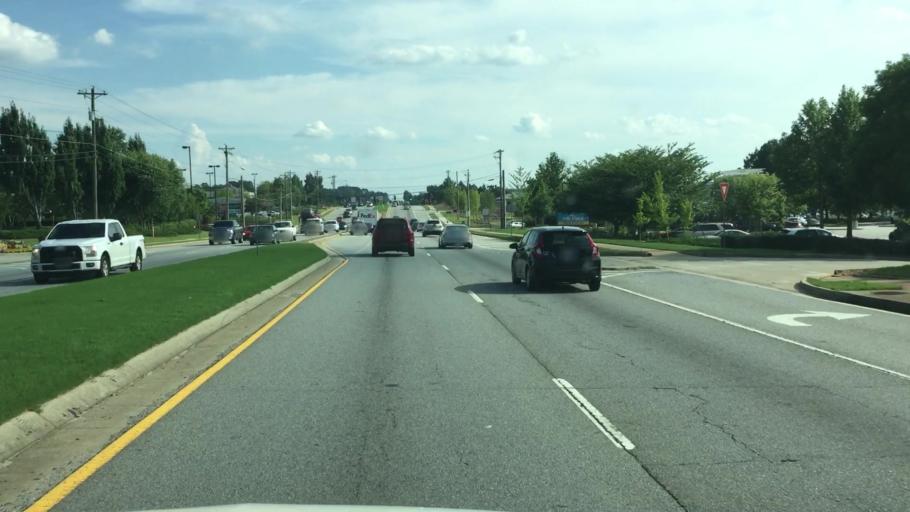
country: US
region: Georgia
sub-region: Gwinnett County
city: Snellville
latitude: 33.8846
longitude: -84.0105
